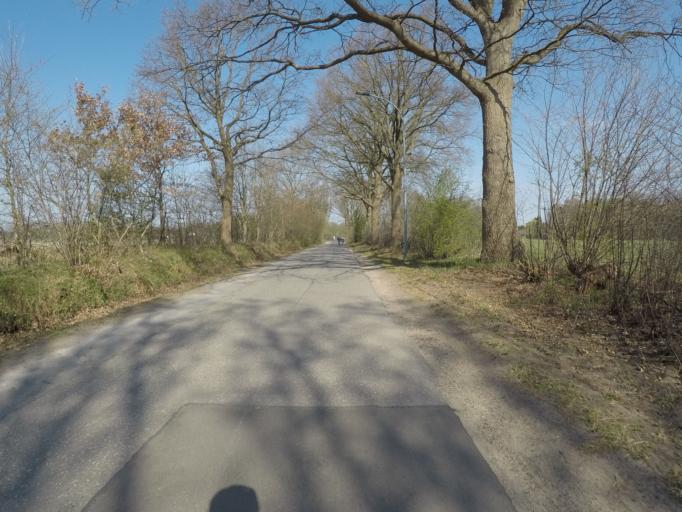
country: DE
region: Schleswig-Holstein
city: Halstenbek
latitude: 53.5925
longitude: 9.8170
